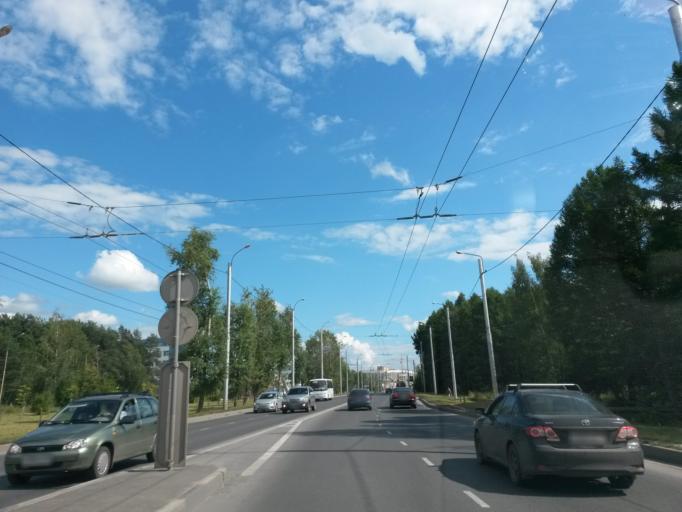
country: RU
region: Ivanovo
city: Kokhma
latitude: 56.9599
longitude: 41.0318
